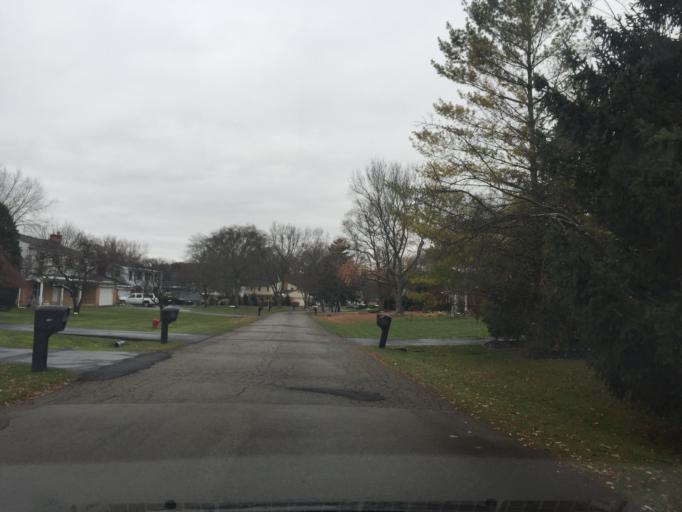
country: US
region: Michigan
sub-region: Oakland County
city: Franklin
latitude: 42.5351
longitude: -83.2897
